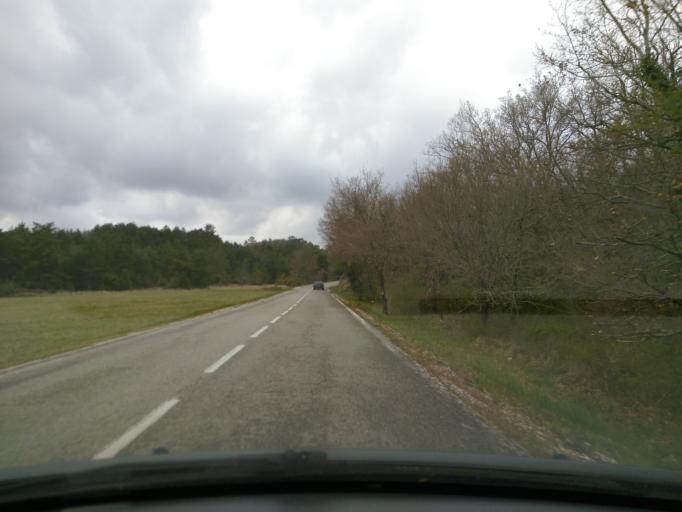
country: FR
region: Languedoc-Roussillon
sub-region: Departement du Gard
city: Barjac
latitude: 44.3559
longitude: 4.3796
